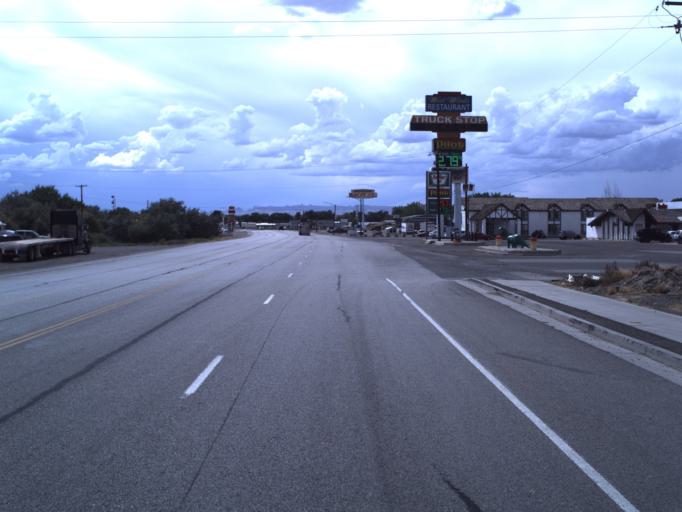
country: US
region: Utah
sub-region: Carbon County
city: East Carbon City
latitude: 38.9948
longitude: -110.1479
